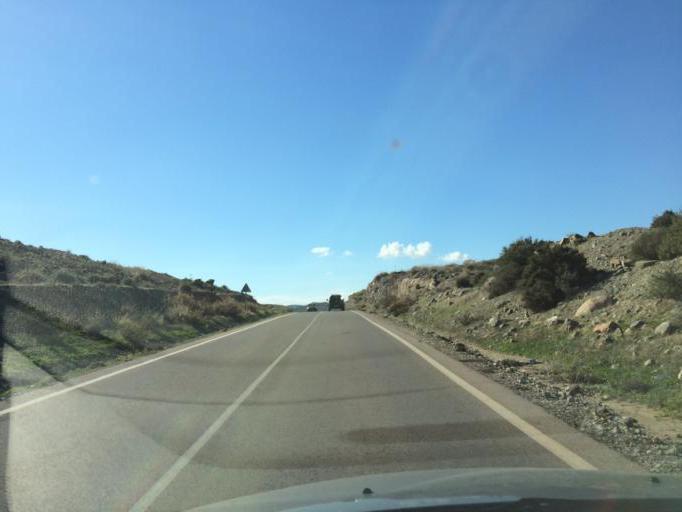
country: ES
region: Andalusia
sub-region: Provincia de Almeria
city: San Jose
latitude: 36.8062
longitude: -2.0883
